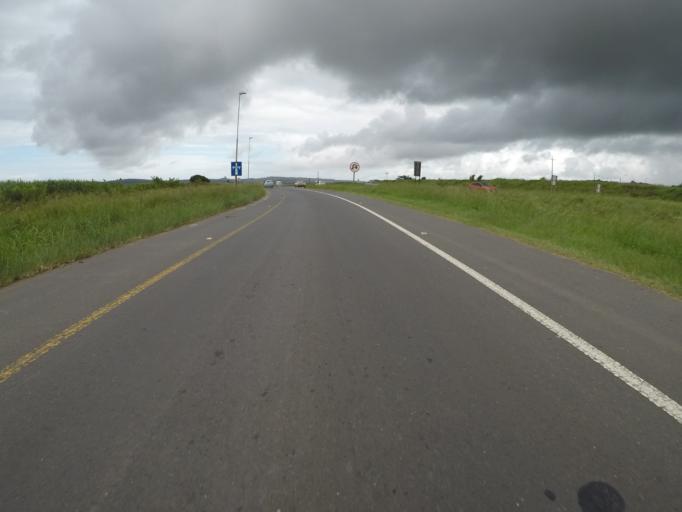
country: ZA
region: KwaZulu-Natal
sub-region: uThungulu District Municipality
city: eSikhawini
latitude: -28.8164
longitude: 31.9133
